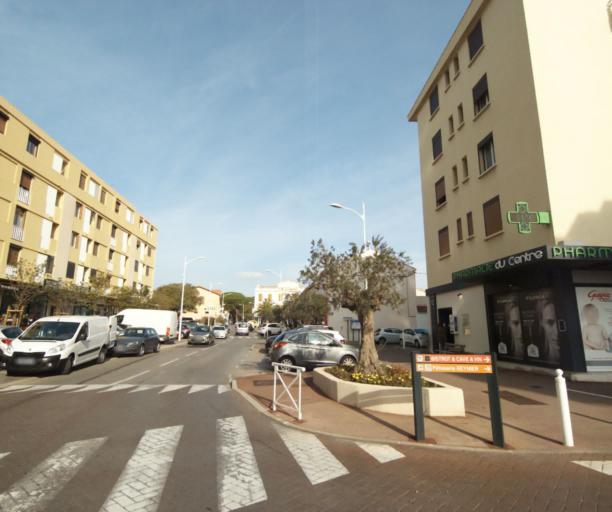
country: FR
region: Provence-Alpes-Cote d'Azur
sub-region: Departement des Bouches-du-Rhone
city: Carry-le-Rouet
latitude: 43.3318
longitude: 5.1521
